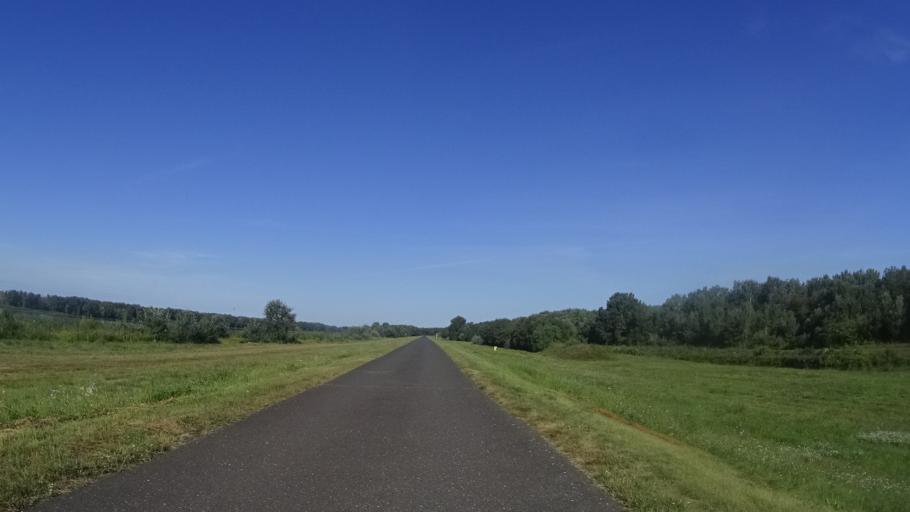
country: HU
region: Gyor-Moson-Sopron
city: Rajka
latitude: 48.0610
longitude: 17.1963
